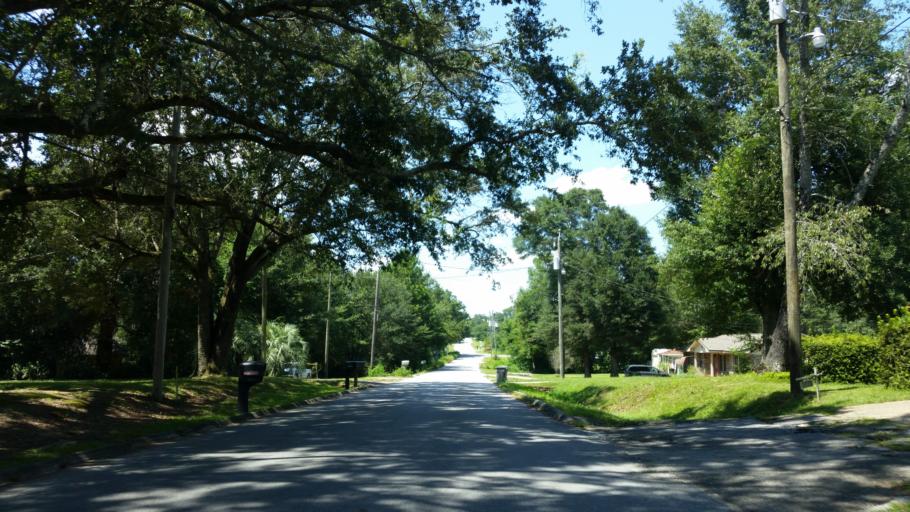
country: US
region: Florida
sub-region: Escambia County
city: Gonzalez
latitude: 30.5688
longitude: -87.2919
